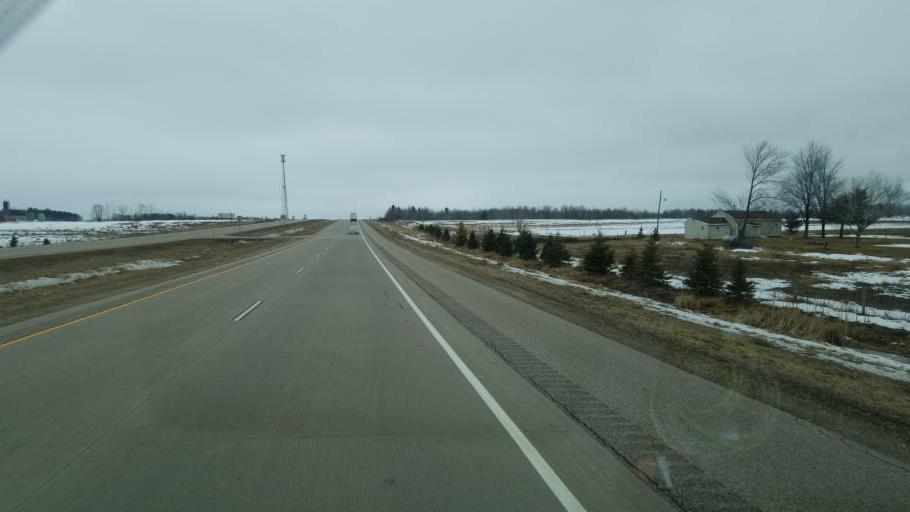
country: US
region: Wisconsin
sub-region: Marathon County
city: Mosinee
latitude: 44.5978
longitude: -89.7857
